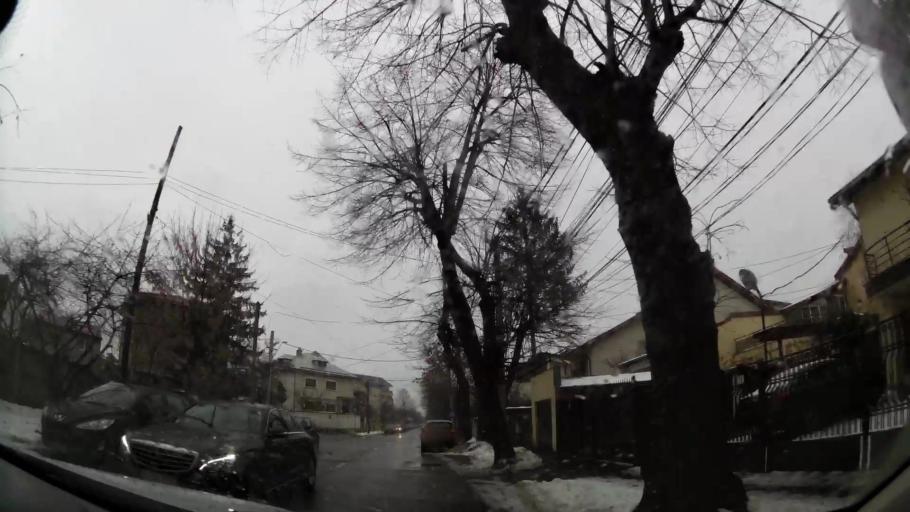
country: RO
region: Ilfov
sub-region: Comuna Chiajna
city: Rosu
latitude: 44.4850
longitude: 26.0412
